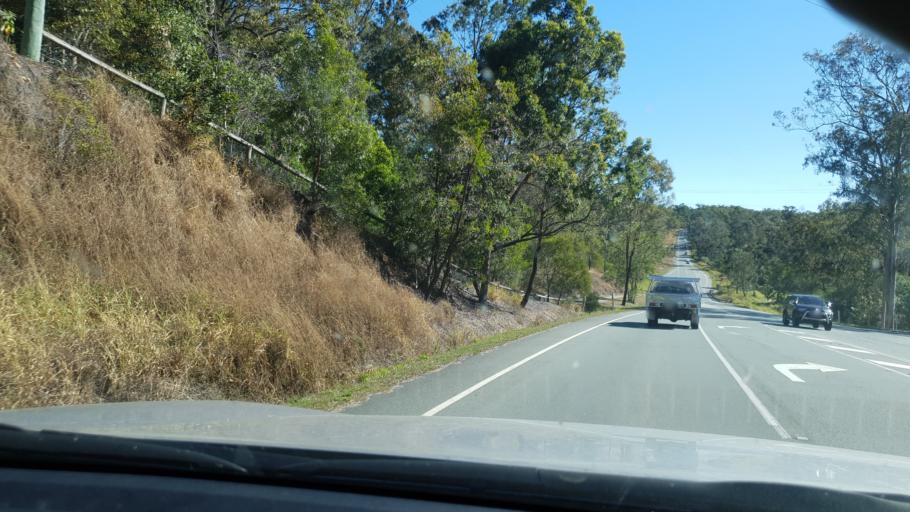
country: AU
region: Queensland
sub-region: Moreton Bay
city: Strathpine
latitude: -27.3293
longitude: 152.9452
